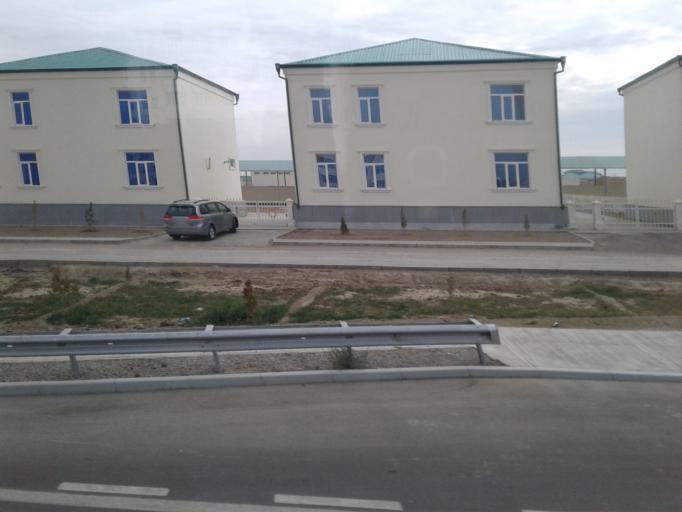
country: TM
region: Lebap
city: Turkmenabat
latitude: 38.9840
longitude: 63.5586
